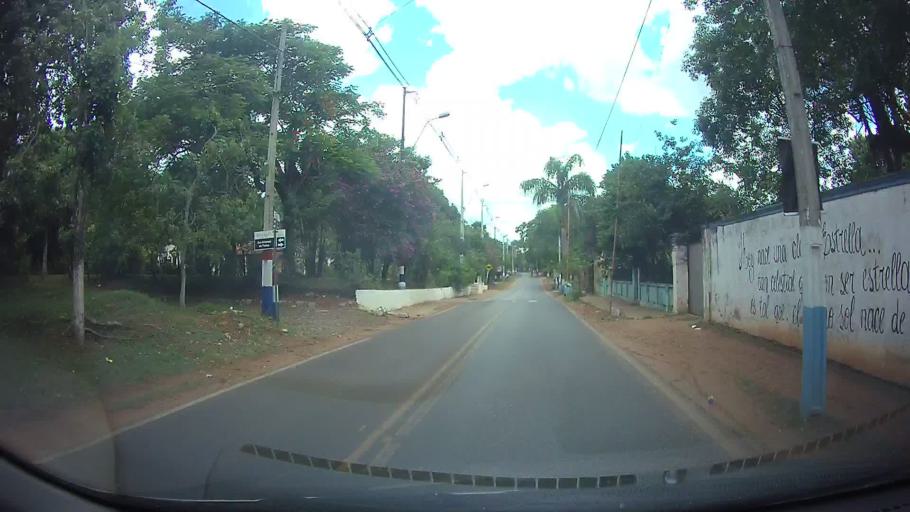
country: PY
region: Central
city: Aregua
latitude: -25.2958
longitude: -57.4408
